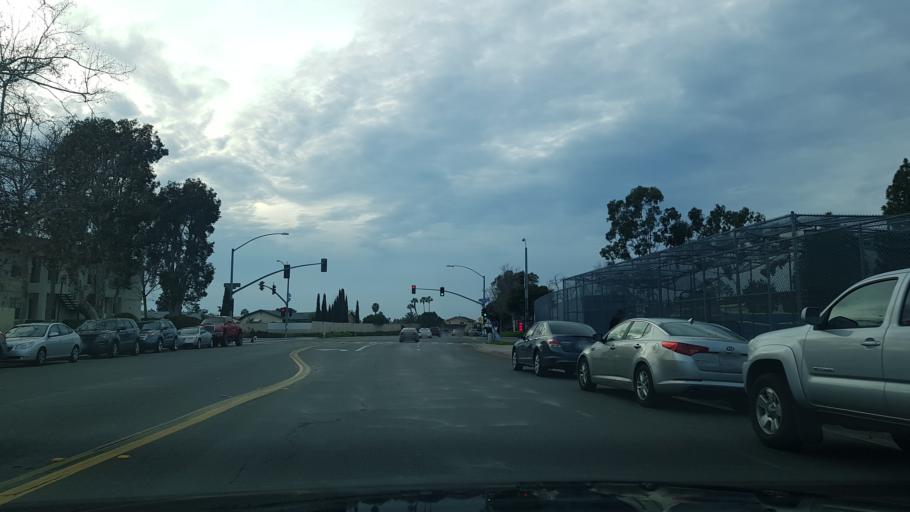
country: US
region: California
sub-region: San Diego County
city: Fairbanks Ranch
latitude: 32.9080
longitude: -117.1442
